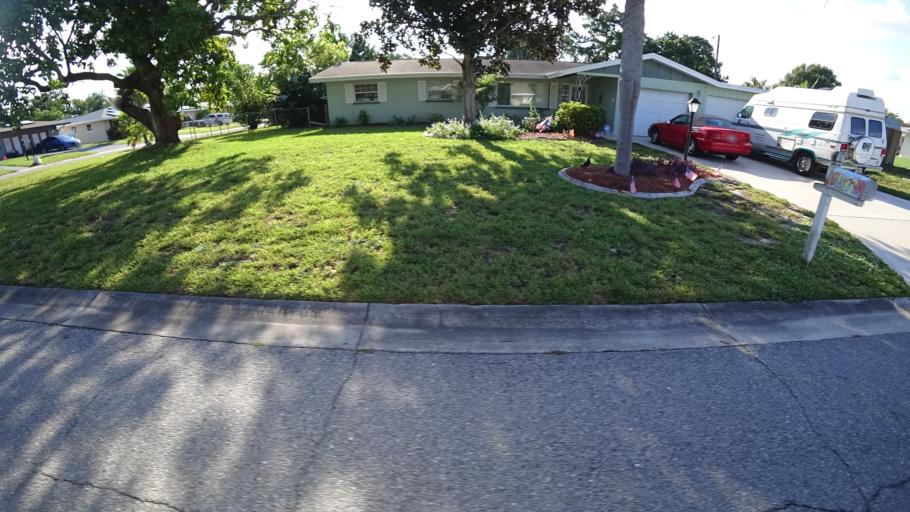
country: US
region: Florida
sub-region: Manatee County
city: South Bradenton
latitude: 27.4765
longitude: -82.5918
